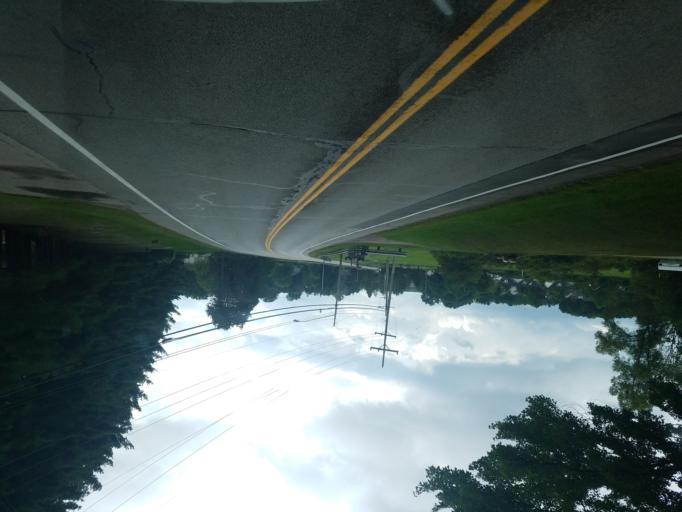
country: US
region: Ohio
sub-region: Geauga County
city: Chardon
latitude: 41.5672
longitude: -81.2033
